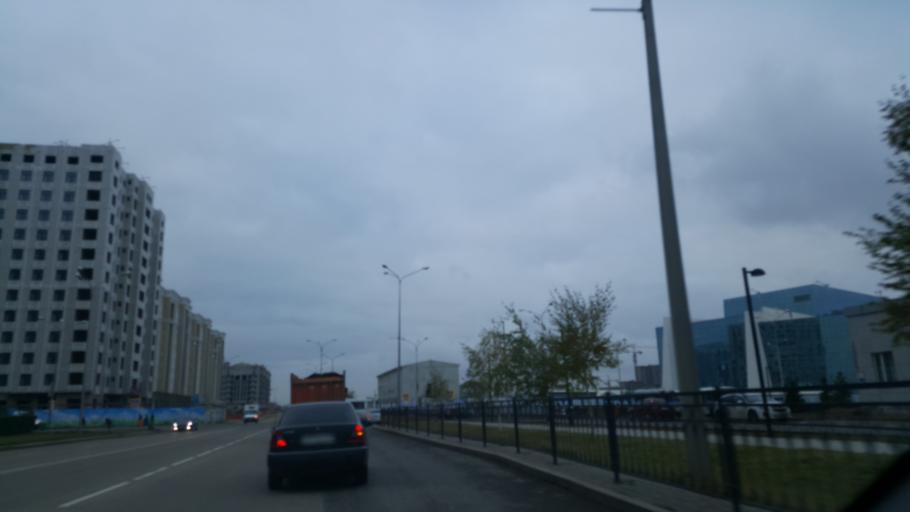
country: KZ
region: Astana Qalasy
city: Astana
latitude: 51.1199
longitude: 71.4737
